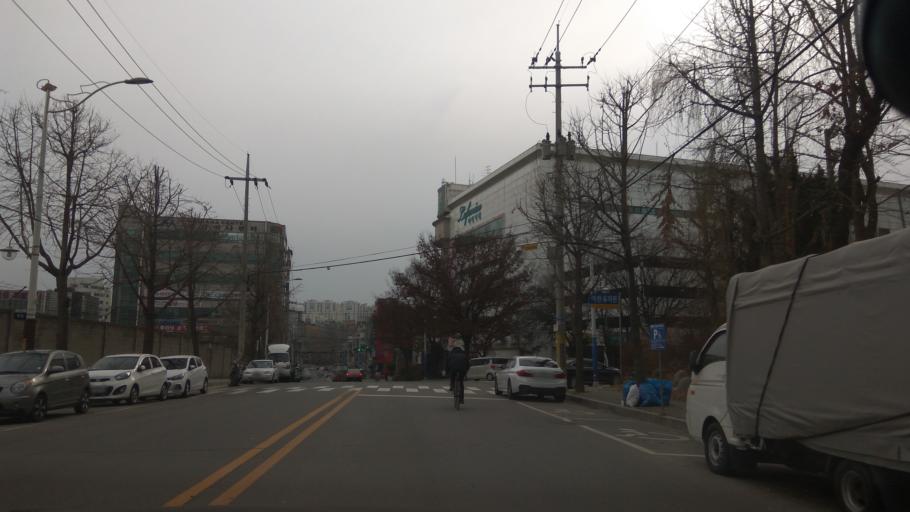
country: KR
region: Incheon
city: Incheon
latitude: 37.4916
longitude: 126.7106
